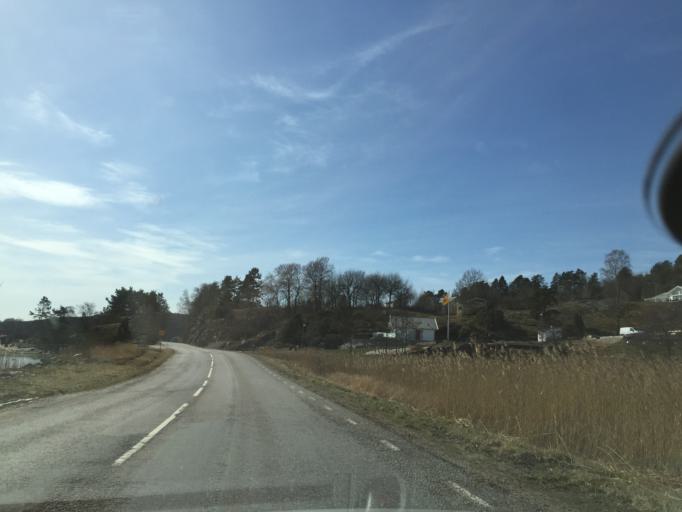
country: SE
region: Vaestra Goetaland
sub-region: Orust
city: Henan
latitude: 58.3412
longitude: 11.7317
